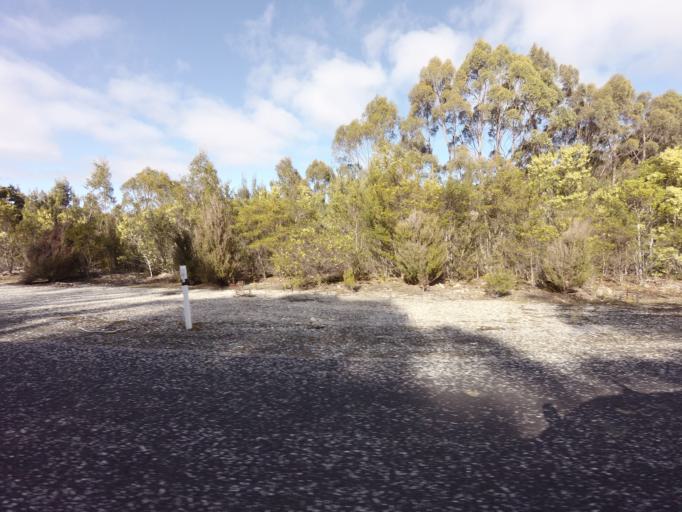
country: AU
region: Tasmania
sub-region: Huon Valley
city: Geeveston
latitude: -42.8210
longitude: 146.1123
